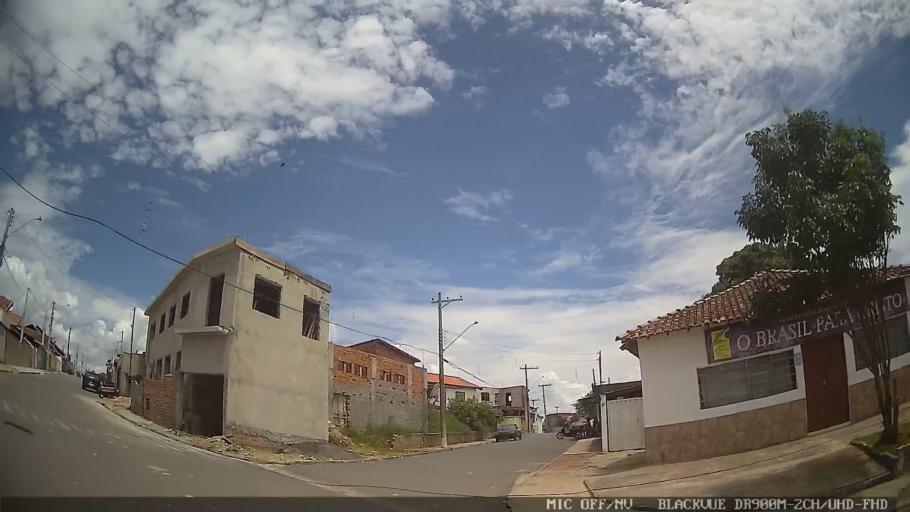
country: BR
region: Sao Paulo
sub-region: Conchas
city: Conchas
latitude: -23.0837
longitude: -47.9756
